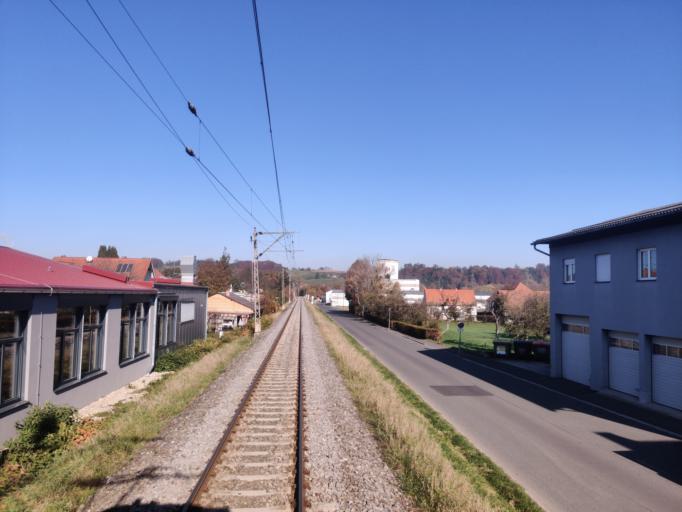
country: AT
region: Styria
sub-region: Politischer Bezirk Suedoststeiermark
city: Feldbach
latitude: 46.9519
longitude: 15.8979
